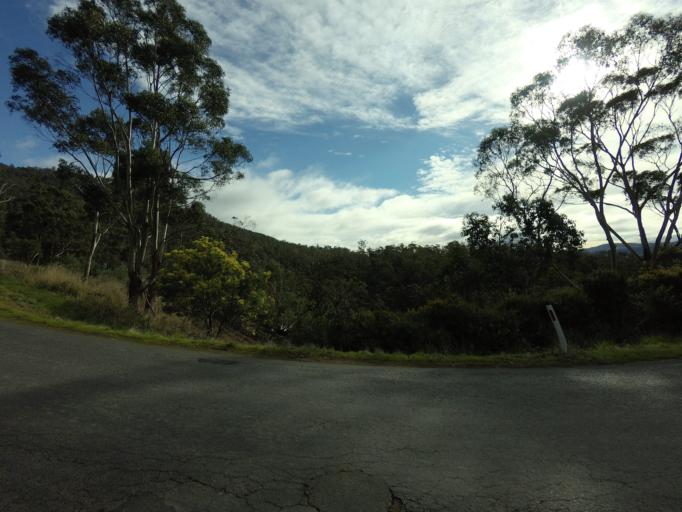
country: AU
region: Tasmania
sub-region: Derwent Valley
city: New Norfolk
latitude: -42.7815
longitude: 146.9540
